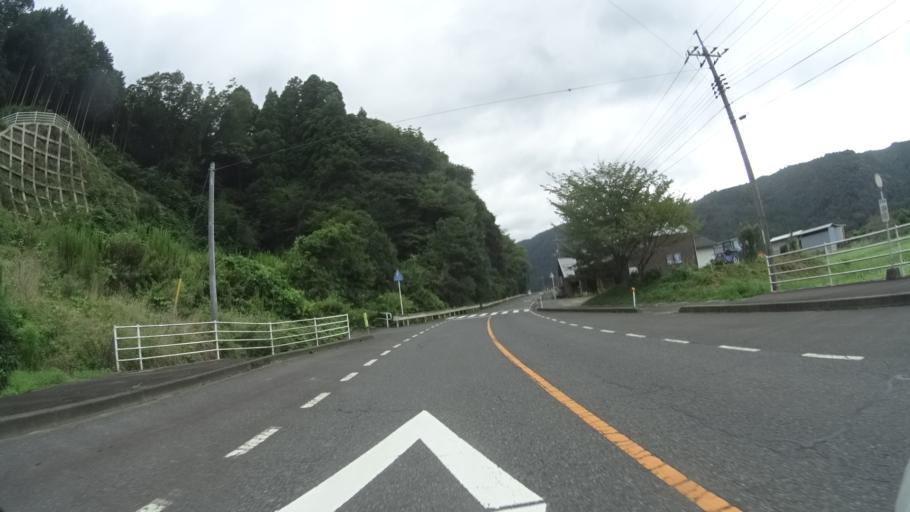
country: JP
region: Tottori
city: Tottori
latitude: 35.4546
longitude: 134.0422
